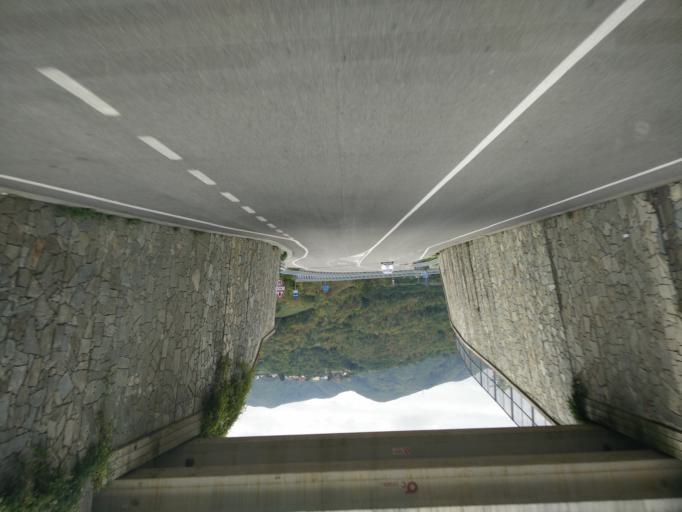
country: IT
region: Tuscany
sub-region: Provincia di Lucca
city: Piazza al Serchio-San Michele
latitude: 44.1793
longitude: 10.3100
